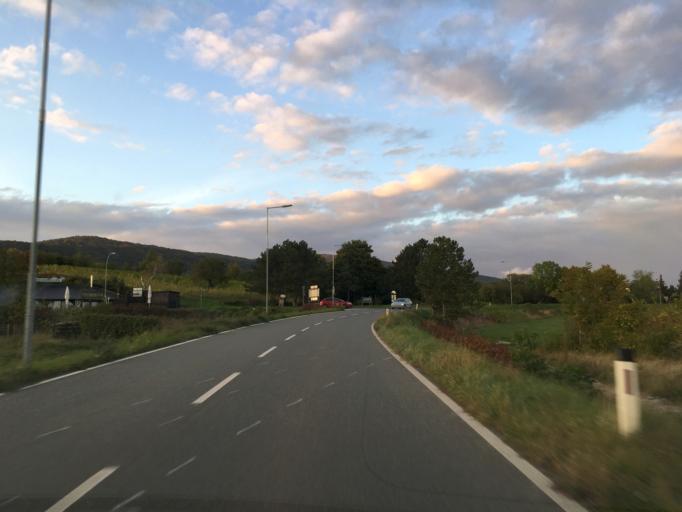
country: AT
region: Lower Austria
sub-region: Politischer Bezirk Baden
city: Pfaffstatten
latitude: 48.0145
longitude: 16.2530
